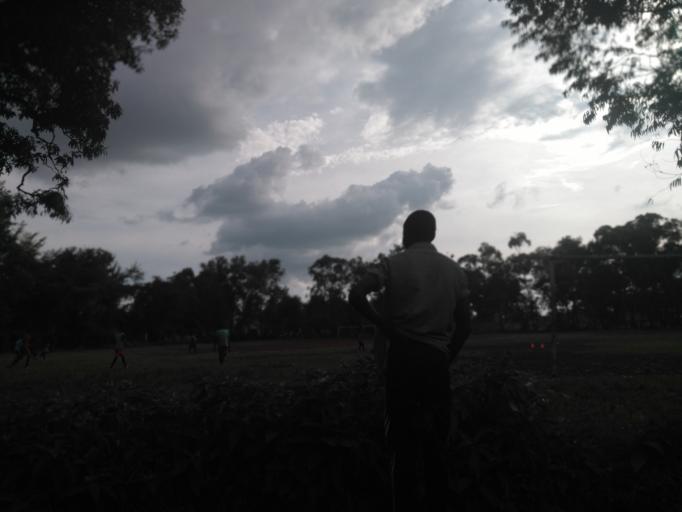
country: UG
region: Eastern Region
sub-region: Jinja District
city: Jinja
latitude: 0.4257
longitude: 33.2048
